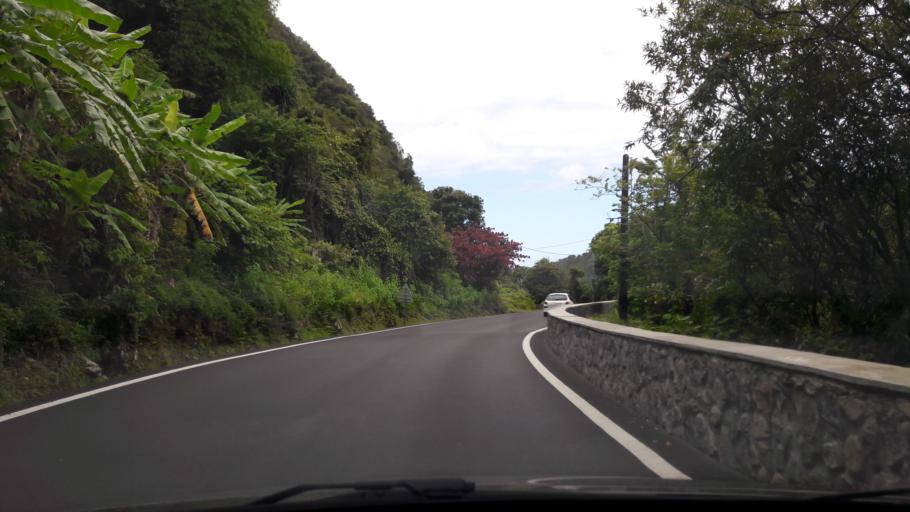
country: RE
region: Reunion
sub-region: Reunion
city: Saint-Andre
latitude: -20.9878
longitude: 55.6191
